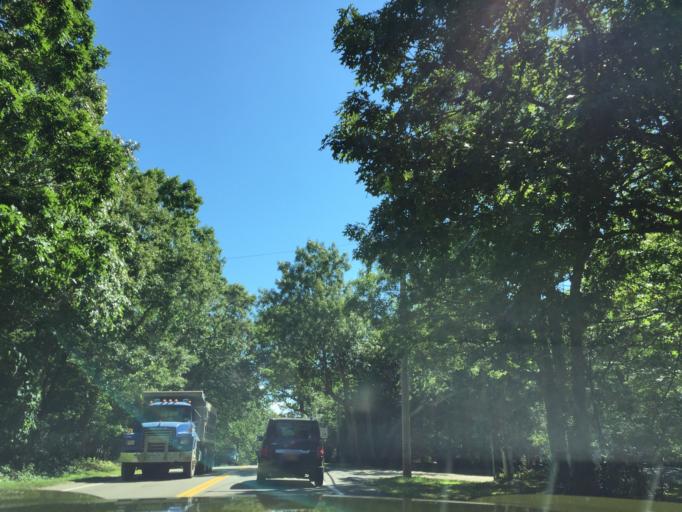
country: US
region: New York
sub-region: Suffolk County
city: North Sea
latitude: 40.9636
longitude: -72.3874
